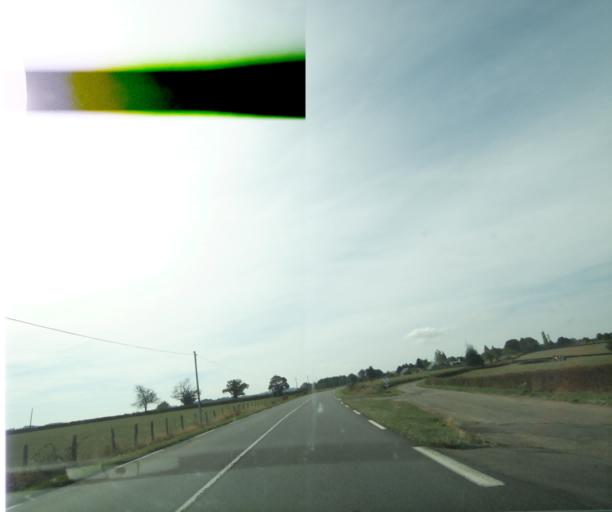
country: FR
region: Auvergne
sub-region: Departement de l'Allier
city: Le Donjon
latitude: 46.3357
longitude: 3.7735
